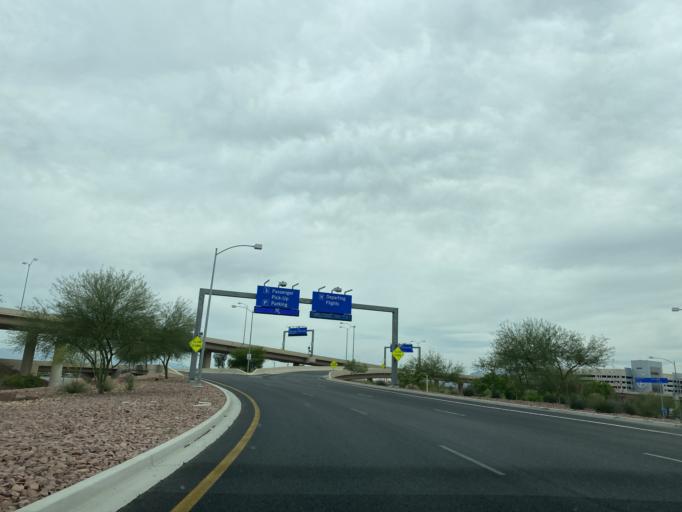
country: US
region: Nevada
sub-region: Clark County
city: Paradise
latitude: 36.0856
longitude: -115.1431
